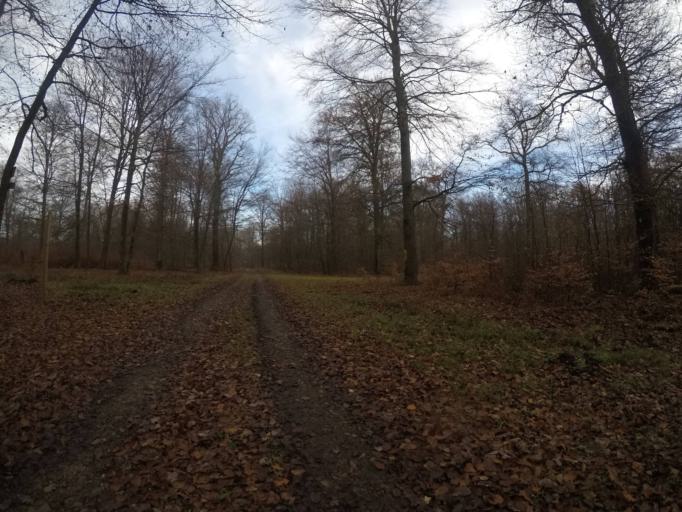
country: BE
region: Wallonia
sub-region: Province du Luxembourg
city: Habay-la-Vieille
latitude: 49.7466
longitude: 5.5929
